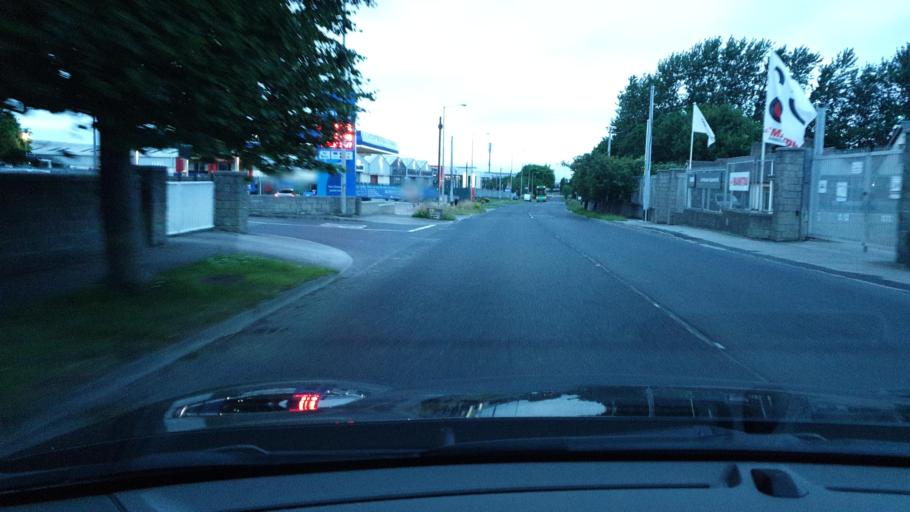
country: IE
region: Leinster
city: Crumlin
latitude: 53.3107
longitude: -6.3544
